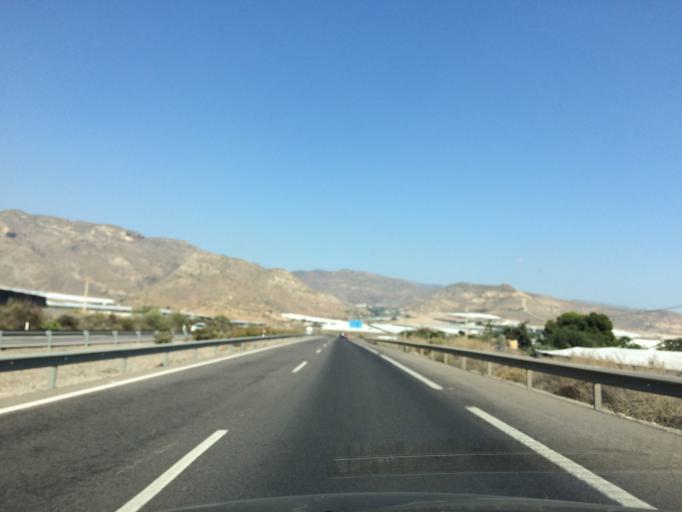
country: ES
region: Andalusia
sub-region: Provincia de Almeria
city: Vicar
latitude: 36.8072
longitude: -2.6696
